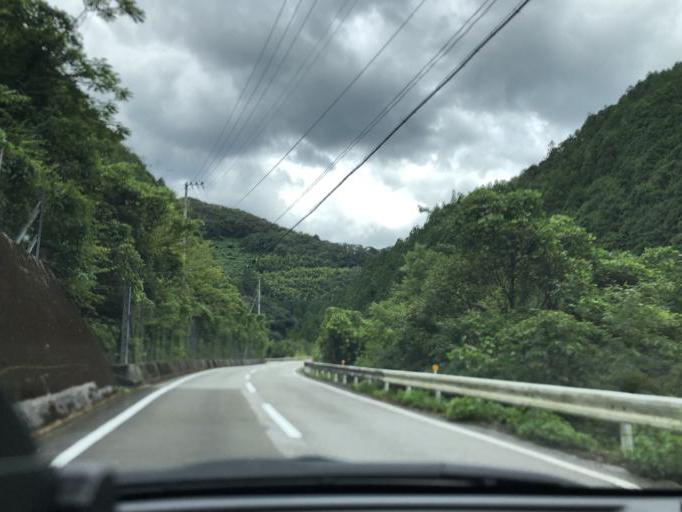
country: JP
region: Kochi
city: Kochi-shi
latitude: 33.6318
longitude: 133.5184
